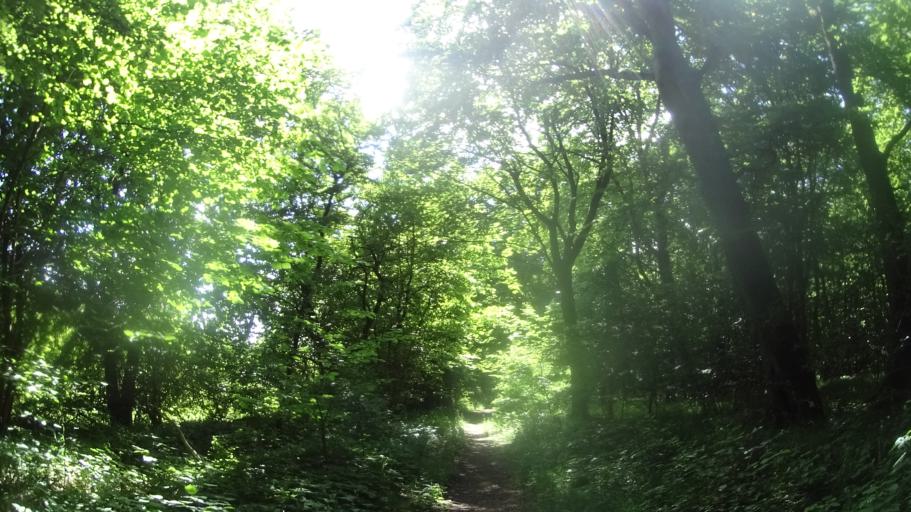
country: DE
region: Lower Saxony
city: Elbe
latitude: 52.1079
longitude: 10.3106
